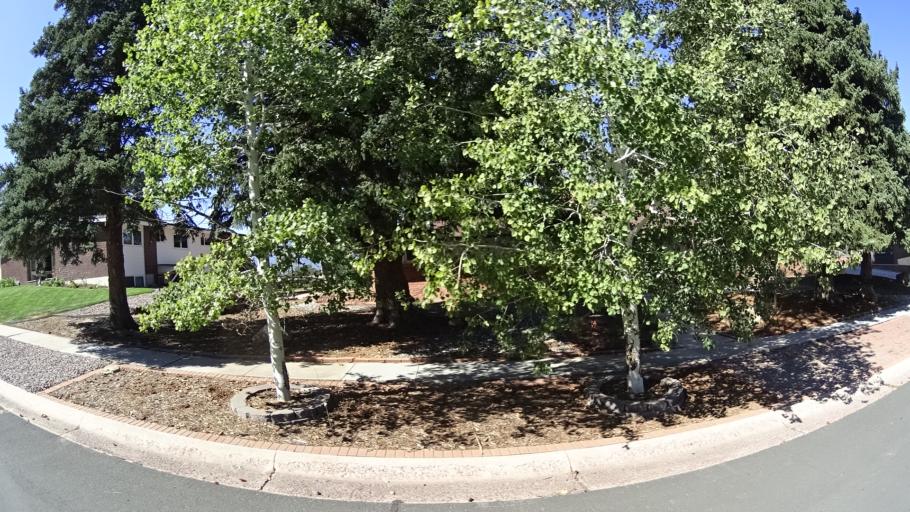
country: US
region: Colorado
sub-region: El Paso County
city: Colorado Springs
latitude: 38.8748
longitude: -104.7861
